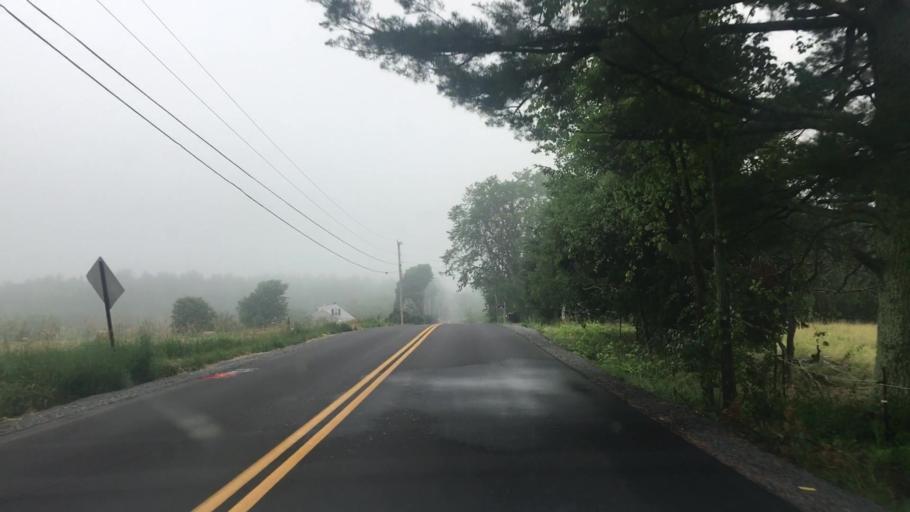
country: US
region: Maine
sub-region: Kennebec County
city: Oakland
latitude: 44.5102
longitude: -69.7079
